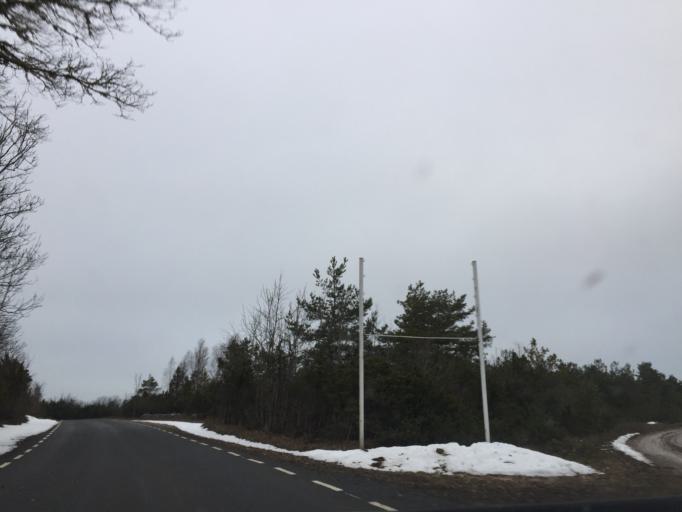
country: EE
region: Saare
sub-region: Kuressaare linn
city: Kuressaare
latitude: 58.5625
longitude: 22.3138
